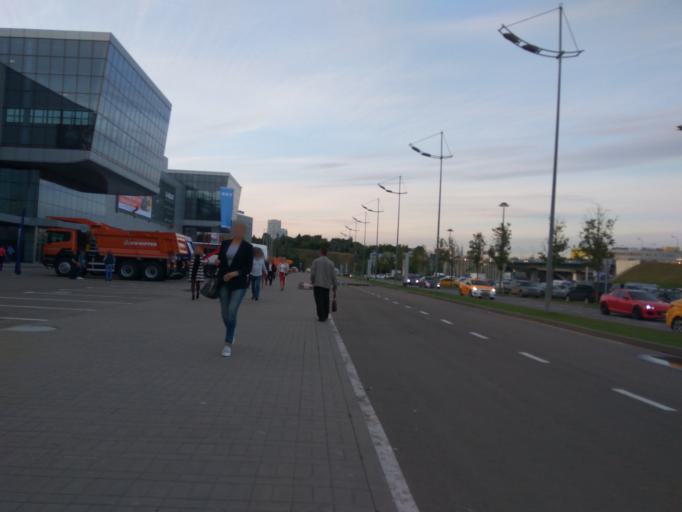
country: RU
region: Moscow
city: Strogino
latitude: 55.8267
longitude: 37.3913
